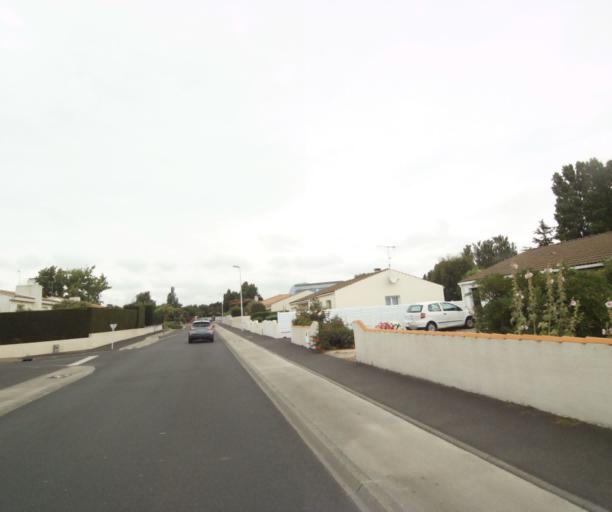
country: FR
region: Pays de la Loire
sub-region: Departement de la Vendee
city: Chateau-d'Olonne
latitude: 46.4877
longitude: -1.7519
